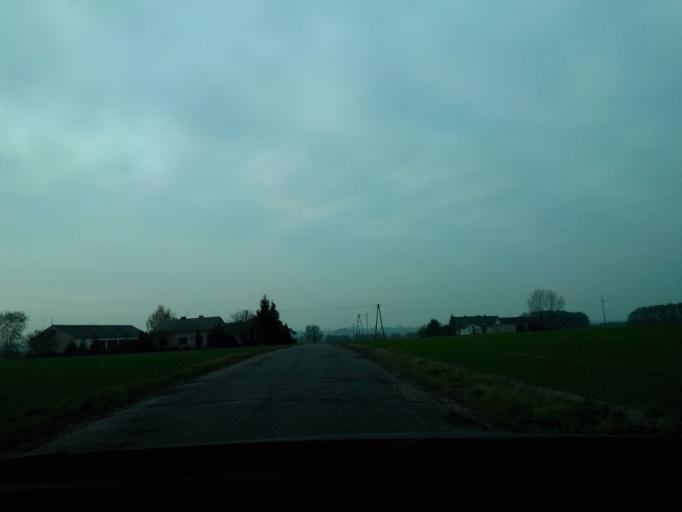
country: PL
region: Kujawsko-Pomorskie
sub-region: Powiat brodnicki
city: Swiedziebnia
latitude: 53.1979
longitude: 19.5616
